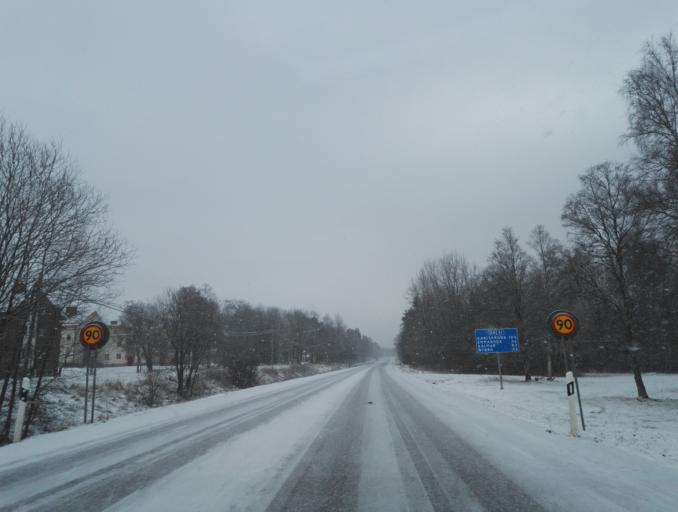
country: SE
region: Kronoberg
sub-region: Uppvidinge Kommun
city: Lenhovda
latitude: 56.9955
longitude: 15.2821
